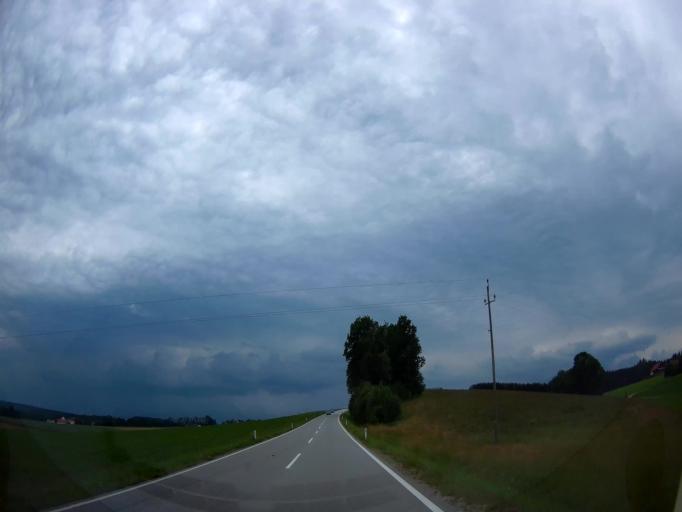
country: AT
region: Upper Austria
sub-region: Politischer Bezirk Braunau am Inn
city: Altheim
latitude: 48.2004
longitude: 13.1595
